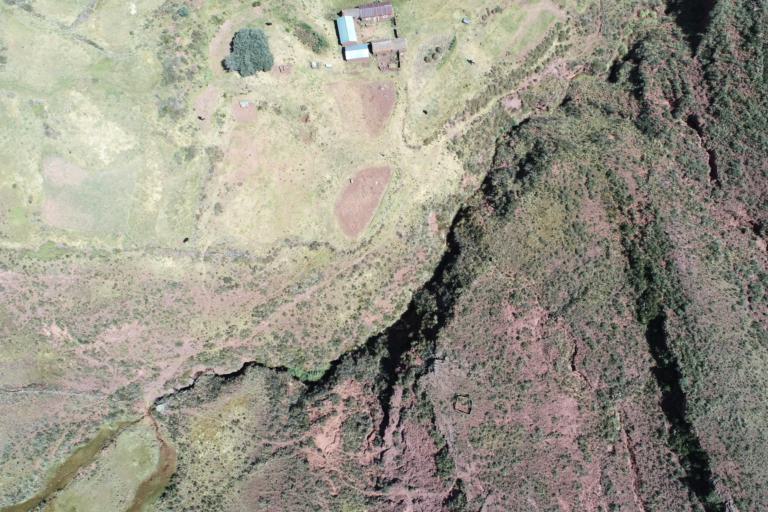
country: BO
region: La Paz
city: Tiahuanaco
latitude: -16.6059
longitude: -68.7616
